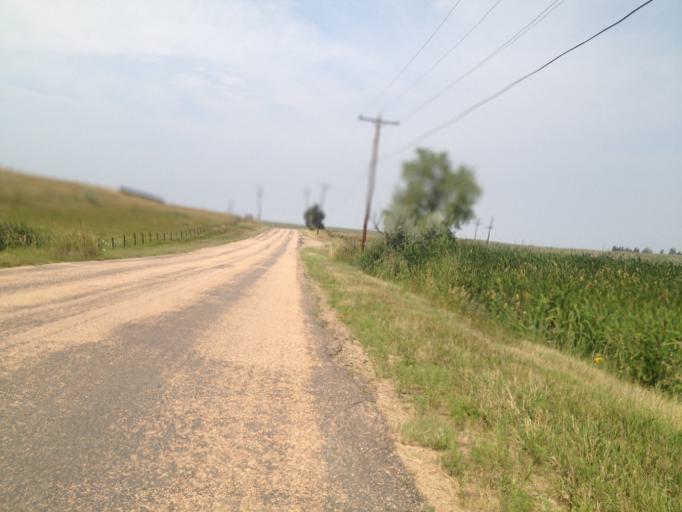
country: US
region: Colorado
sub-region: Boulder County
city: Superior
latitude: 39.9556
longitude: -105.1988
